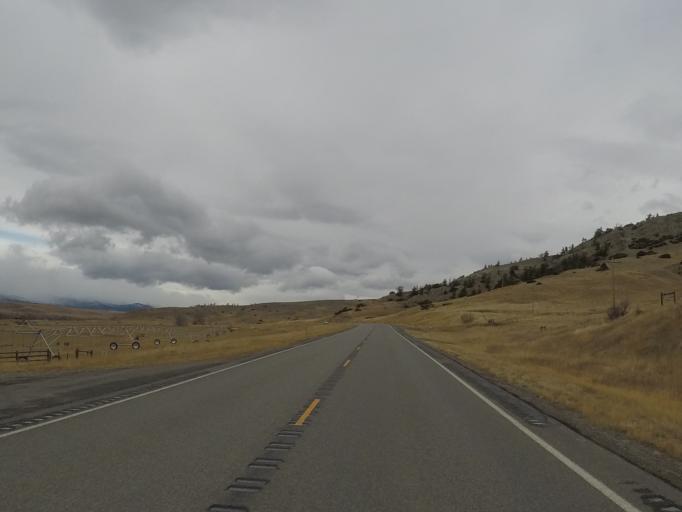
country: US
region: Montana
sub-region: Sweet Grass County
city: Big Timber
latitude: 45.8933
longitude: -109.9614
